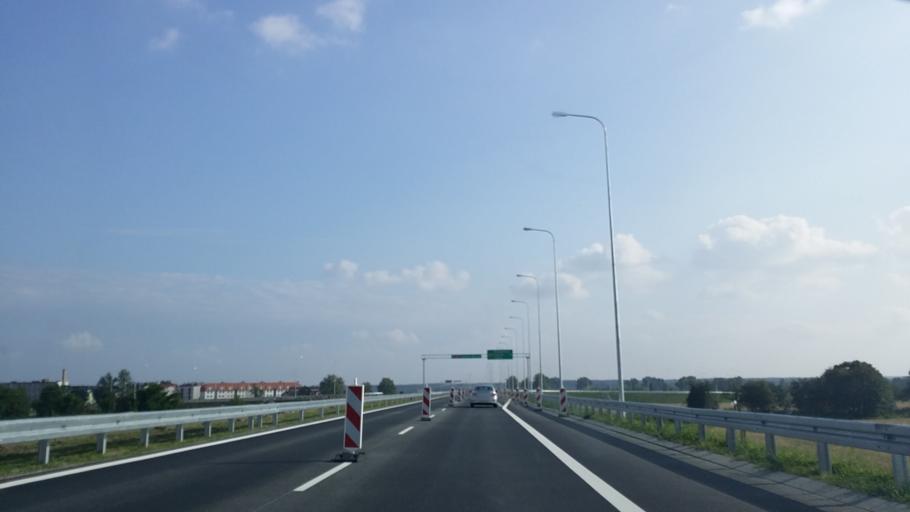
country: PL
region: Lubusz
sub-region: Powiat miedzyrzecki
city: Miedzyrzecz
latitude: 52.4468
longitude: 15.5603
